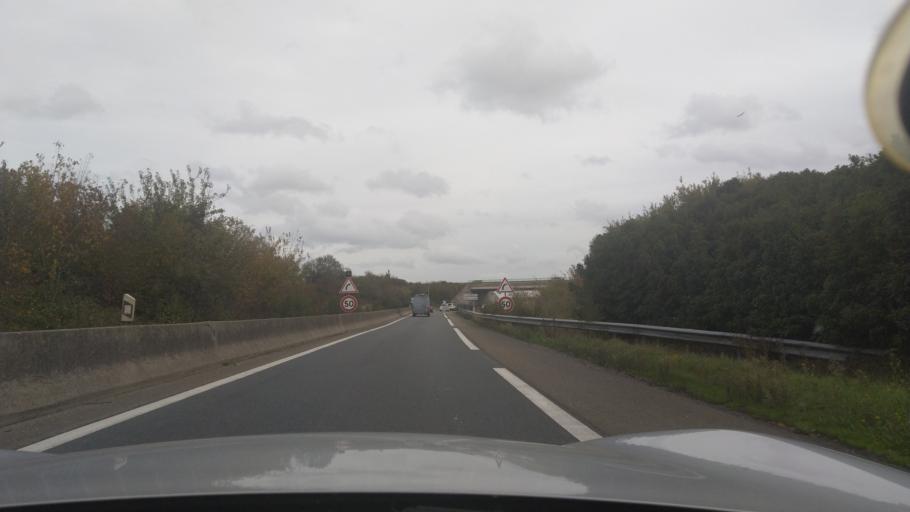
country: FR
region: Ile-de-France
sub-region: Departement du Val-d'Oise
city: Roissy-en-France
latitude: 49.0284
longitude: 2.5347
